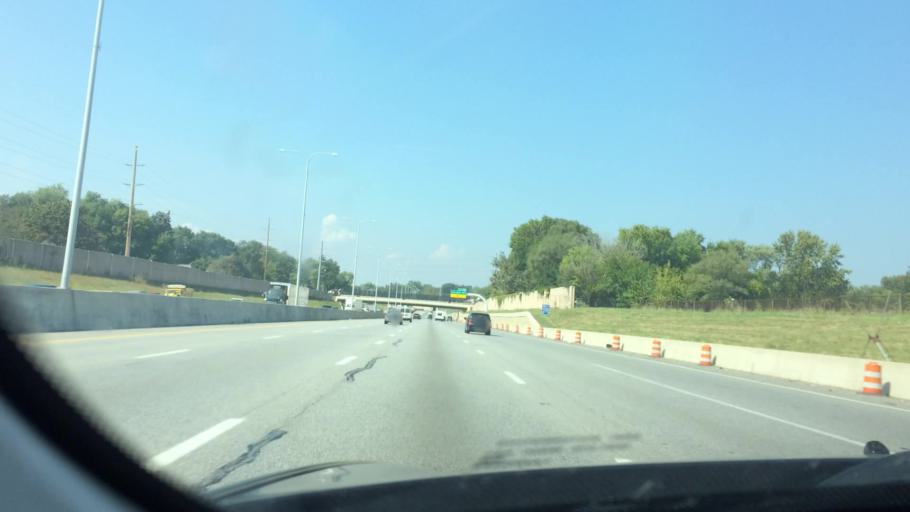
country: US
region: Ohio
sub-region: Lucas County
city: Toledo
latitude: 41.6816
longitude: -83.5951
